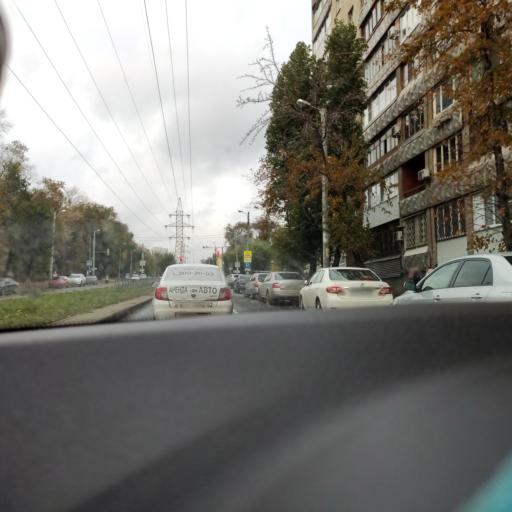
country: RU
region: Samara
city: Samara
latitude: 53.1985
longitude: 50.2143
